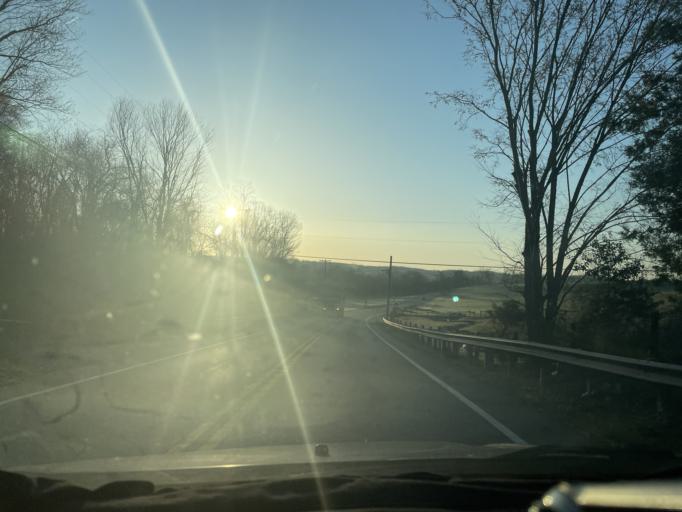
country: US
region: Maryland
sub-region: Frederick County
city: Adamstown
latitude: 39.2536
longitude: -77.4506
